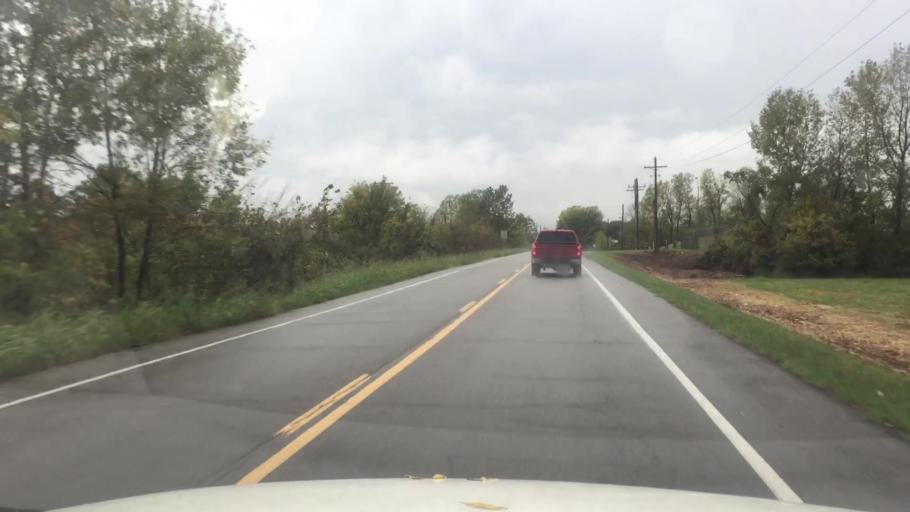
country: US
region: Missouri
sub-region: Boone County
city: Columbia
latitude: 38.8859
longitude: -92.4409
